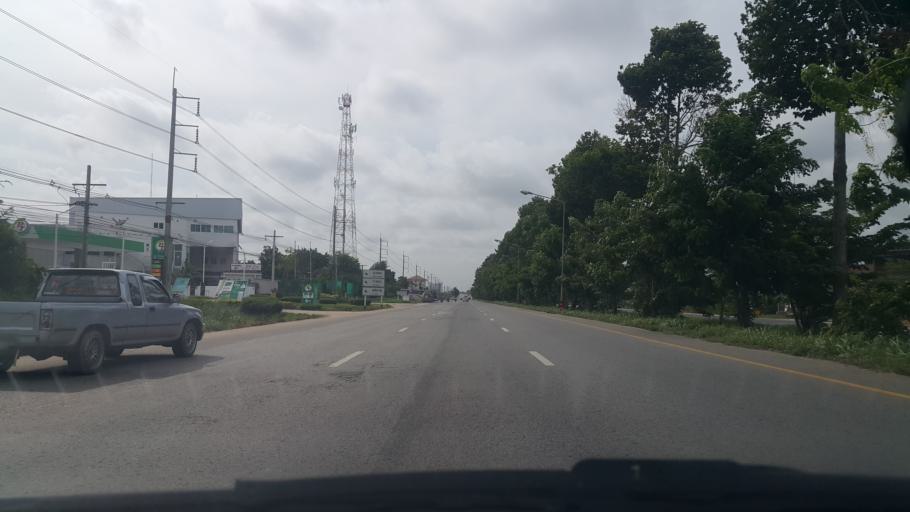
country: TH
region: Rayong
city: Rayong
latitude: 12.6757
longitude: 101.3032
